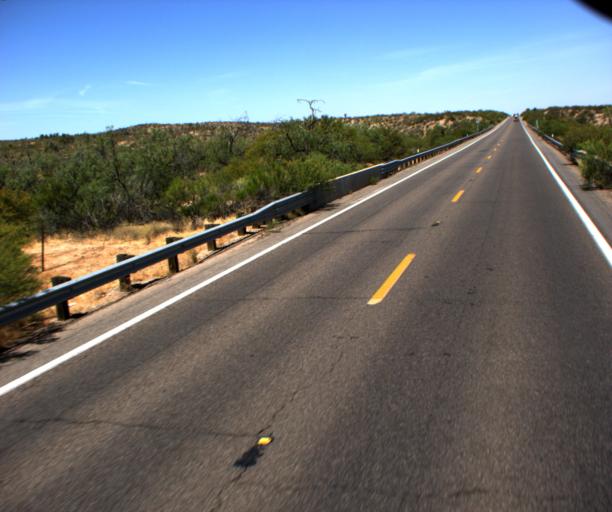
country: US
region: Arizona
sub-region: Gila County
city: Peridot
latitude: 33.3273
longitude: -110.5582
